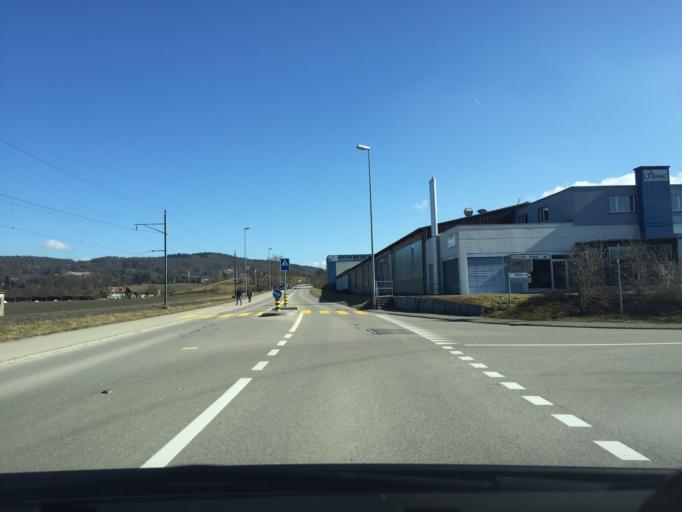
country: CH
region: Thurgau
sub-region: Frauenfeld District
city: Diessenhofen
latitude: 47.6867
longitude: 8.7296
